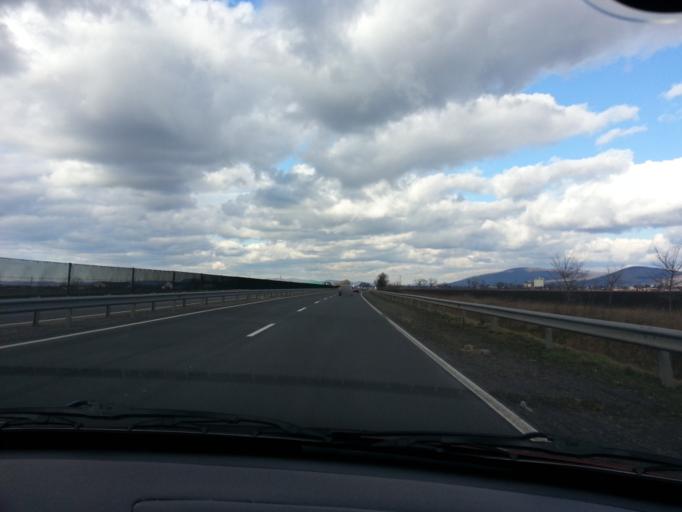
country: HU
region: Heves
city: Lorinci
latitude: 47.7414
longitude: 19.6630
